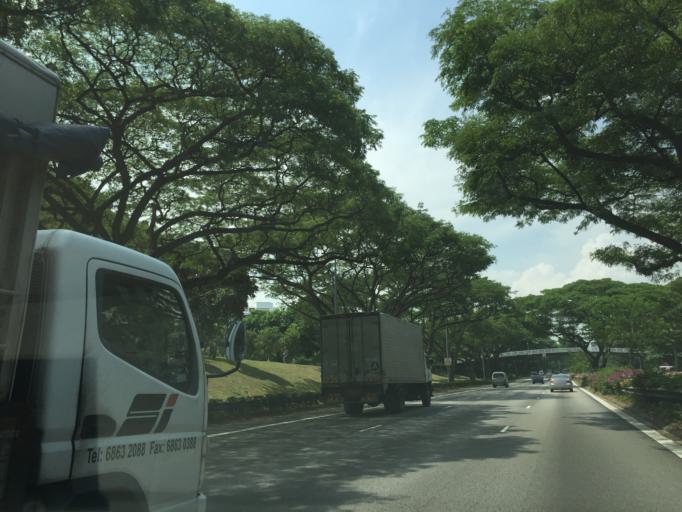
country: SG
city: Singapore
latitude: 1.3332
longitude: 103.9212
